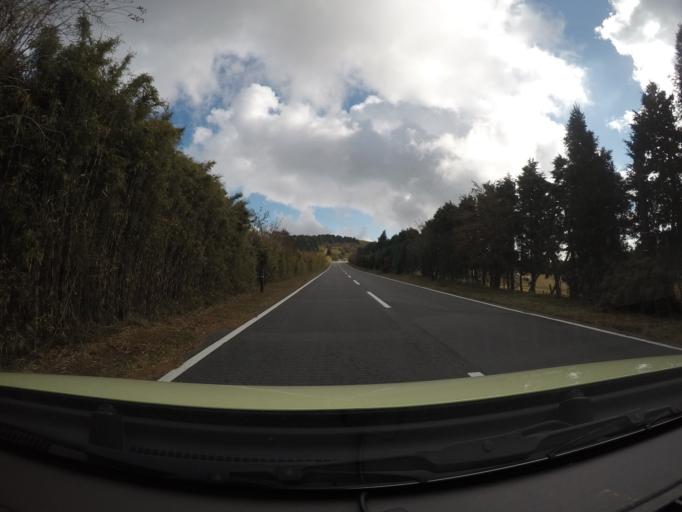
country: JP
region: Kanagawa
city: Hakone
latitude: 35.1872
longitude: 139.0035
